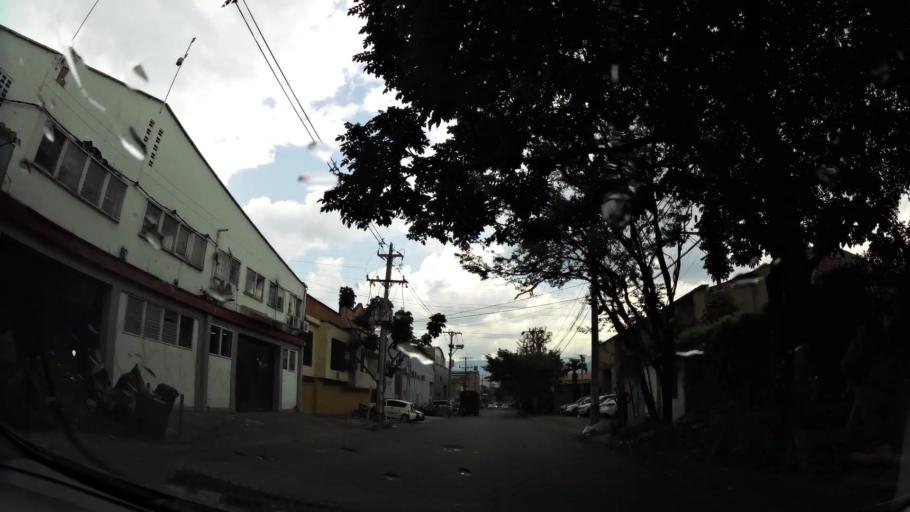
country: CO
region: Antioquia
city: Itagui
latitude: 6.1794
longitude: -75.5965
